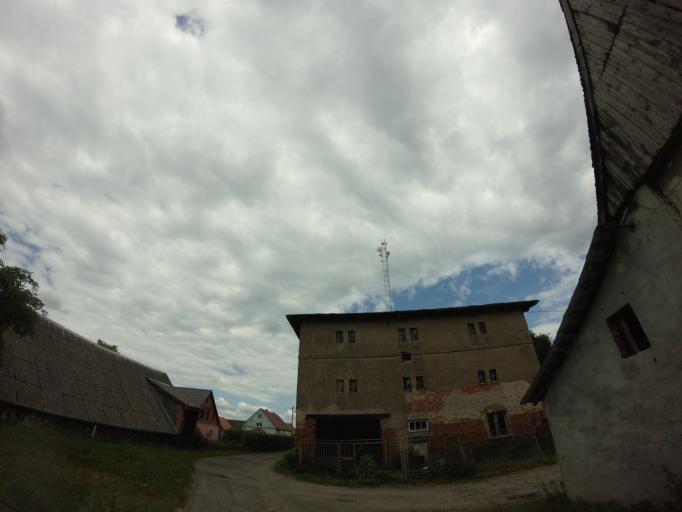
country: PL
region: West Pomeranian Voivodeship
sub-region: Powiat choszczenski
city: Recz
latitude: 53.1863
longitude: 15.5857
